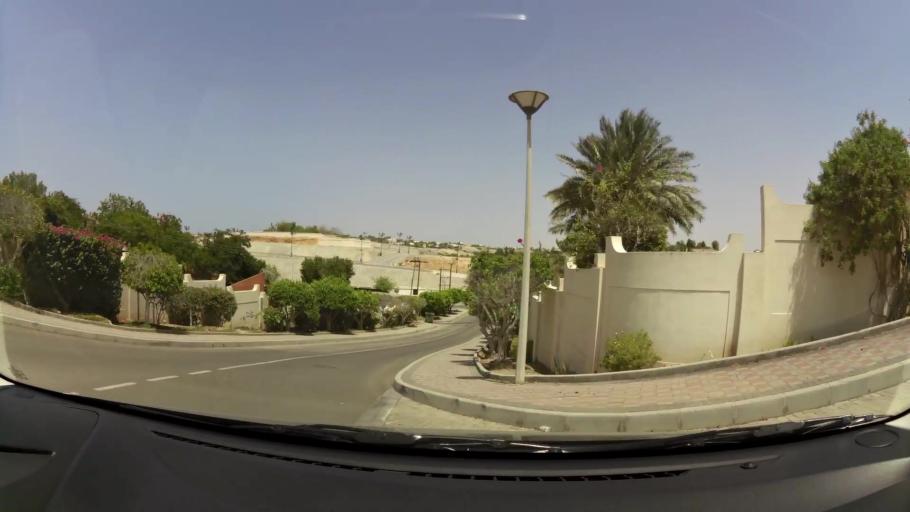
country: OM
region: Muhafazat Masqat
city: Muscat
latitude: 23.6358
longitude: 58.4872
